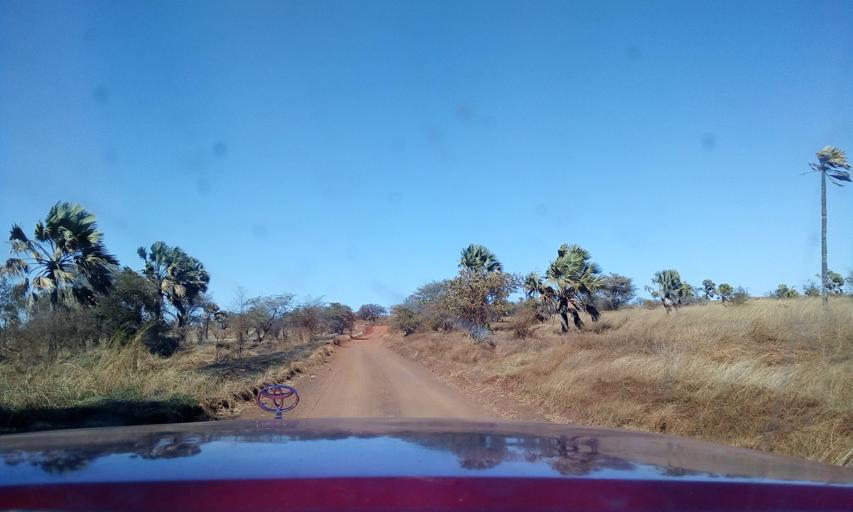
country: MG
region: Boeny
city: Mahajanga
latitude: -15.8755
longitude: 46.1352
